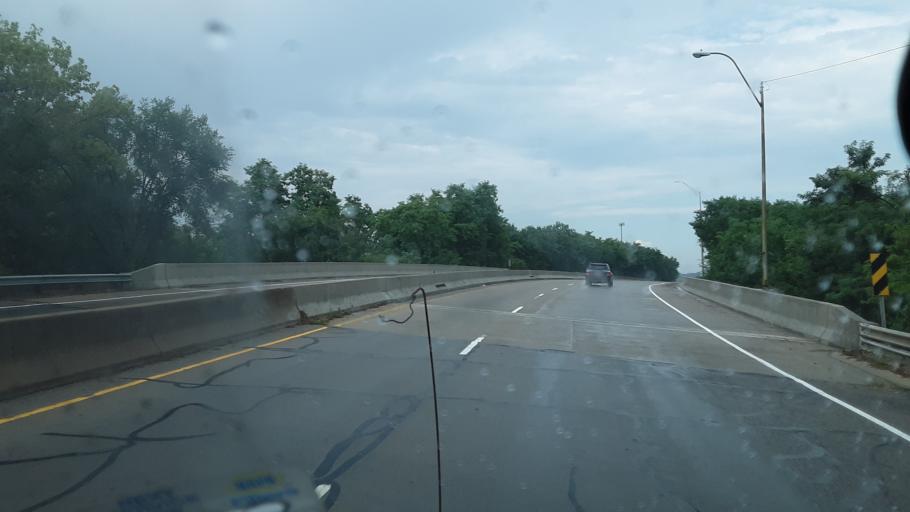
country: US
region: Ohio
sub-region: Fairfield County
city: Lancaster
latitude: 39.7079
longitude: -82.6047
